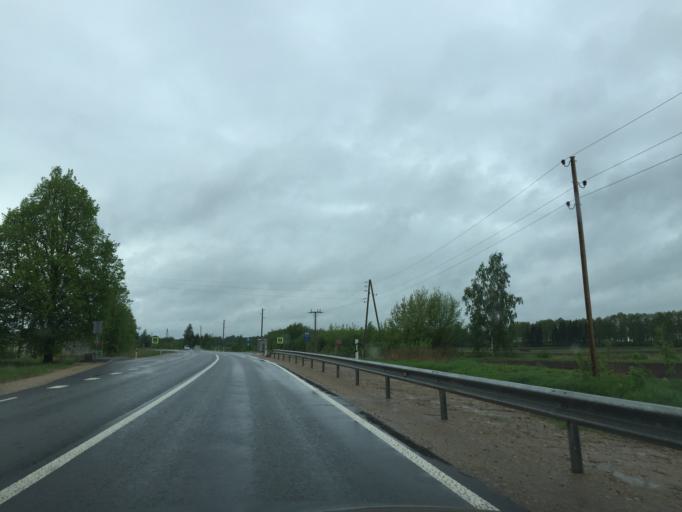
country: LV
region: Lielvarde
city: Lielvarde
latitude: 56.7007
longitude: 24.8835
